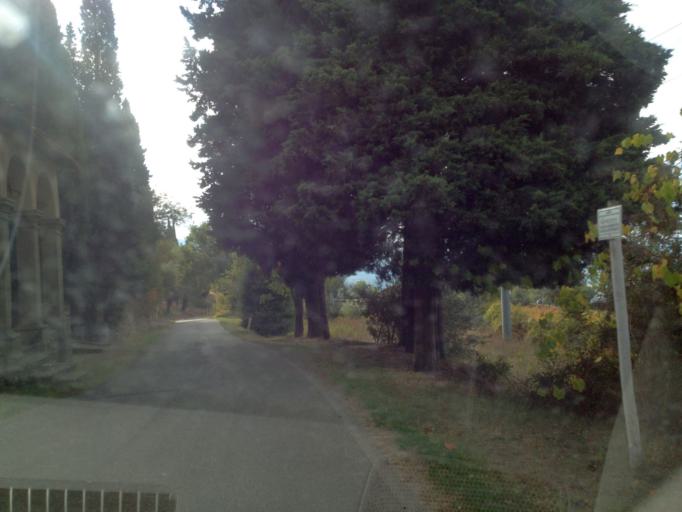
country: IT
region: Tuscany
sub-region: Province of Florence
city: Montebonello
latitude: 43.8591
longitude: 11.5076
